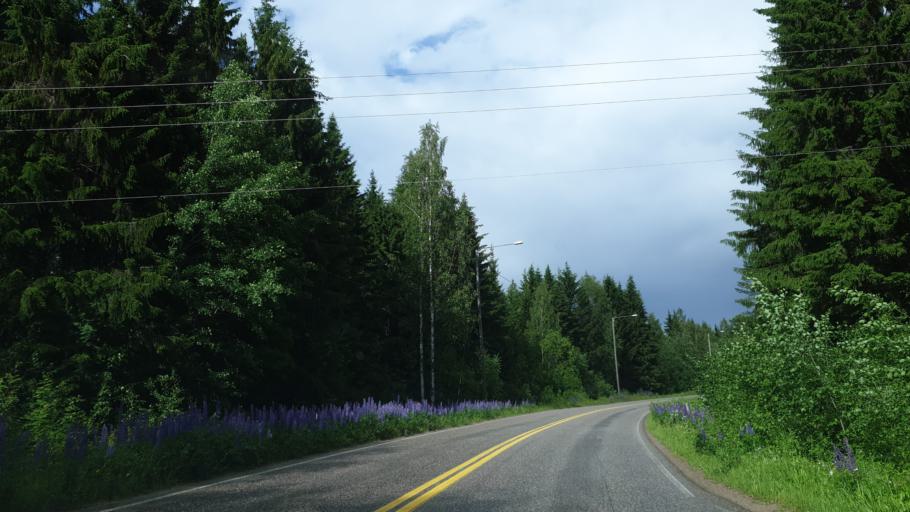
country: FI
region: Northern Savo
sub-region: Kuopio
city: Kuopio
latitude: 62.9056
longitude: 27.8440
